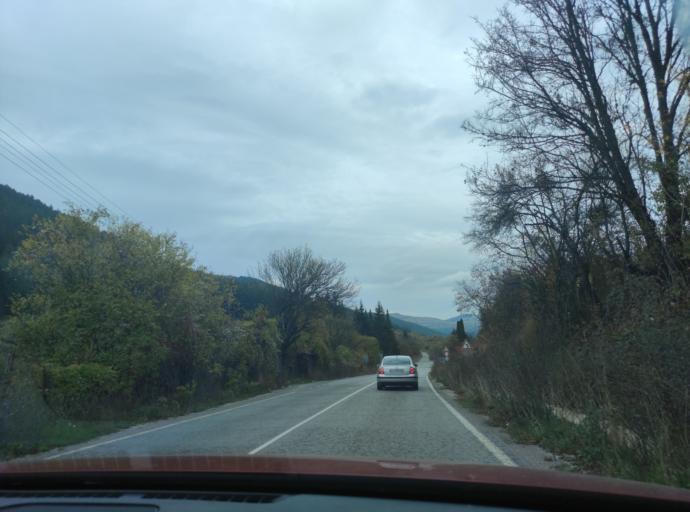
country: BG
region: Sofiya
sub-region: Obshtina Godech
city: Godech
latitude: 43.0374
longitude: 23.1372
